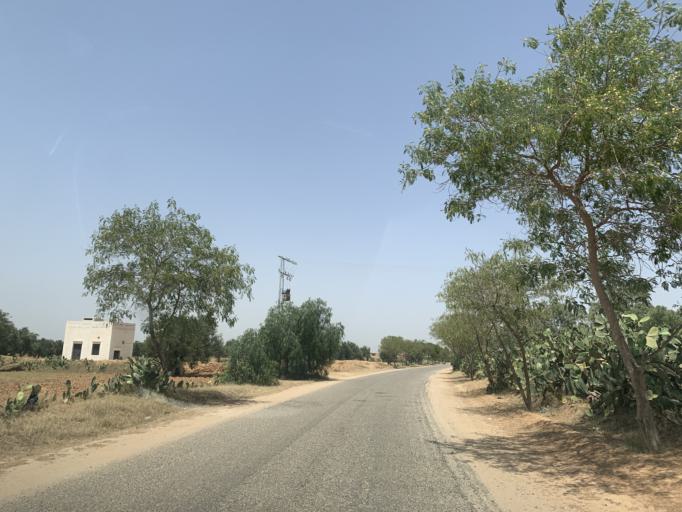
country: TN
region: Al Mahdiyah
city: Shurban
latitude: 35.1878
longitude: 10.2440
